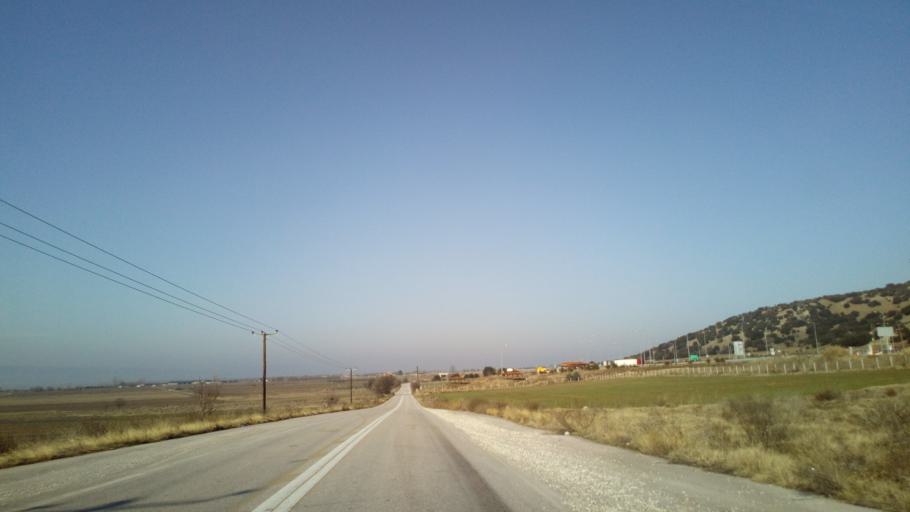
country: GR
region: Central Macedonia
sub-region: Nomos Thessalonikis
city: Kolchikon
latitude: 40.7058
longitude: 23.1918
